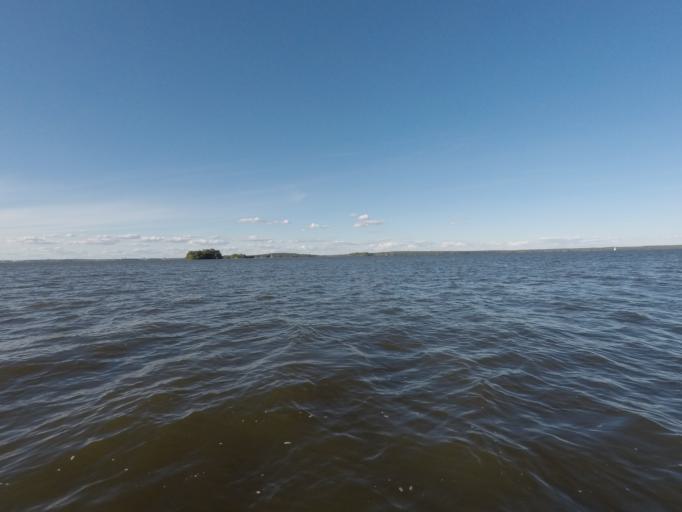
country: SE
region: Vaestmanland
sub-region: Vasteras
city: Vasteras
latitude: 59.5177
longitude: 16.5881
